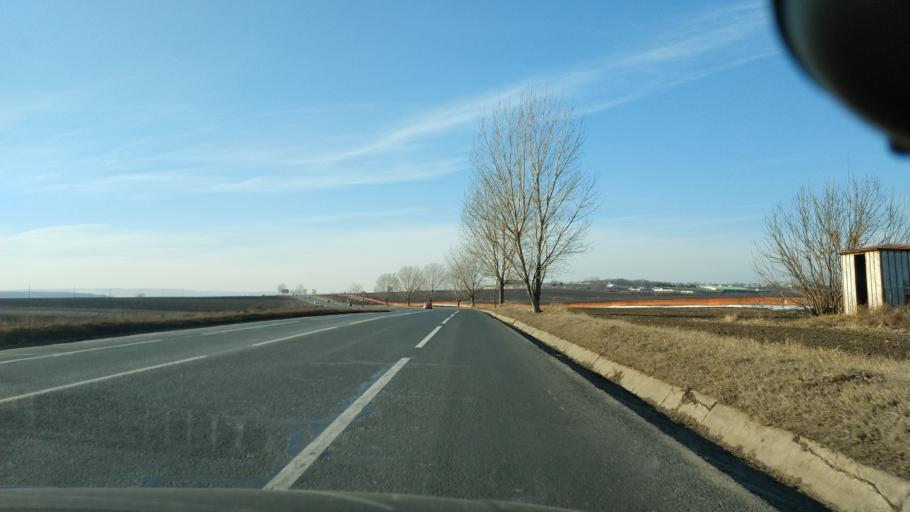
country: RO
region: Iasi
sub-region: Comuna Ion Neculce
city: Razboieni
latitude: 47.2216
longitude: 27.0867
